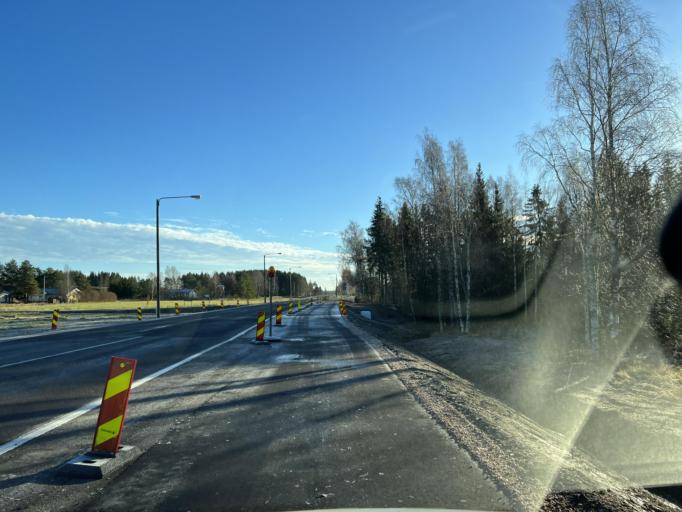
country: FI
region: Northern Ostrobothnia
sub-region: Nivala-Haapajaervi
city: Nivala
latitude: 63.9489
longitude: 24.9226
